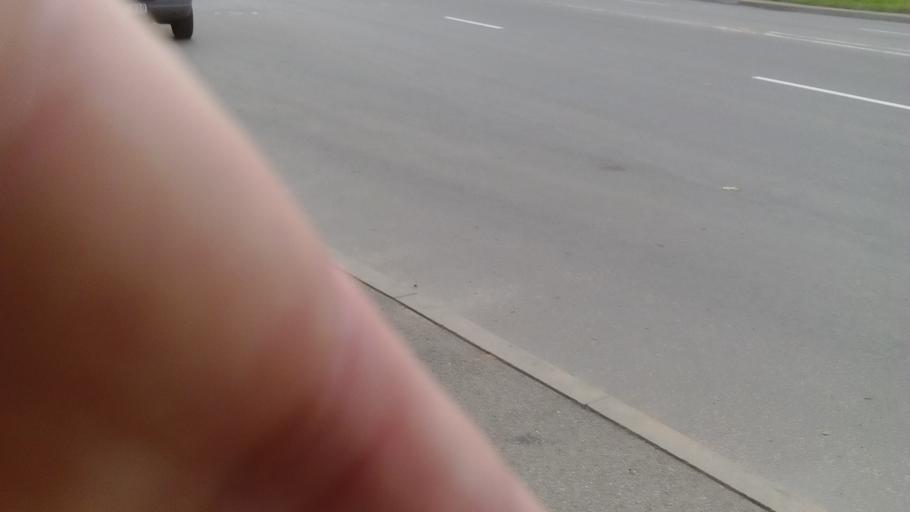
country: LT
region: Alytaus apskritis
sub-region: Alytus
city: Alytus
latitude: 54.4240
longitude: 24.0331
